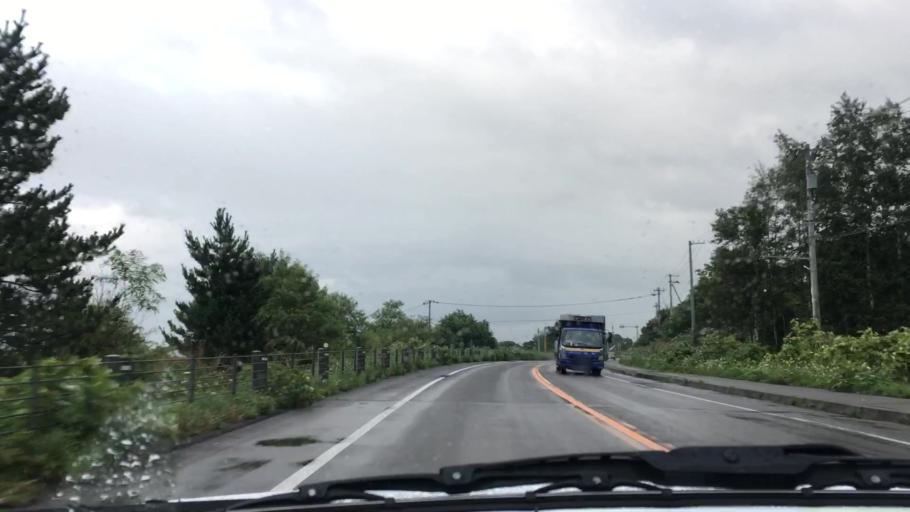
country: JP
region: Hokkaido
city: Nanae
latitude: 42.1784
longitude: 140.4460
